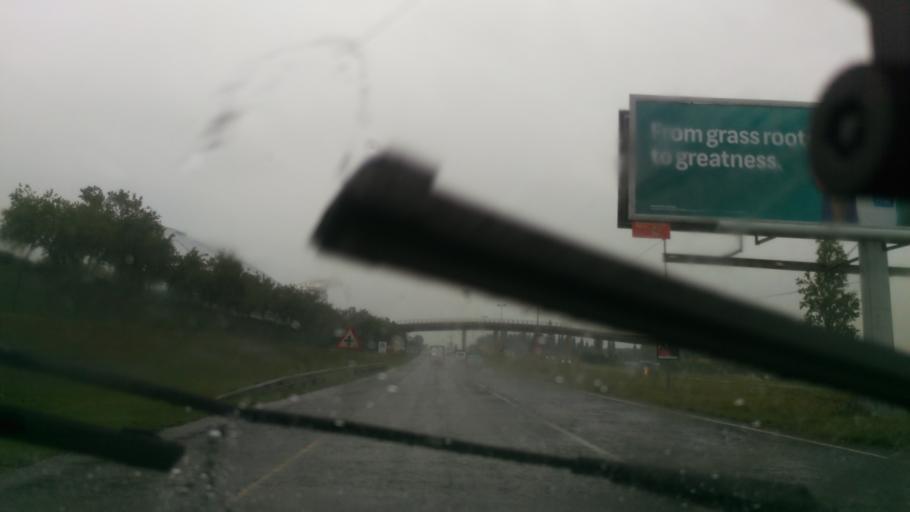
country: ZA
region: Gauteng
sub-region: West Rand District Municipality
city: Muldersdriseloop
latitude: -26.0605
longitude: 27.9433
